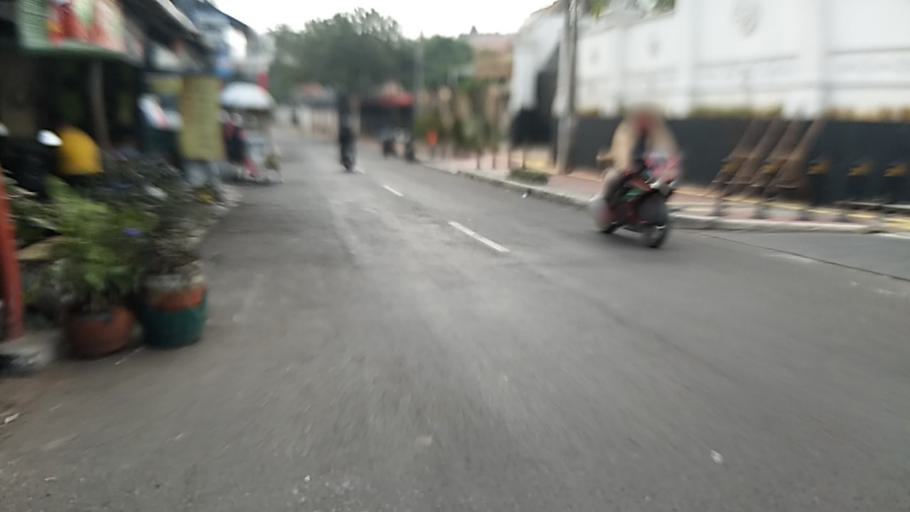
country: ID
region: Jakarta Raya
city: Jakarta
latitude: -6.2275
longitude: 106.8527
